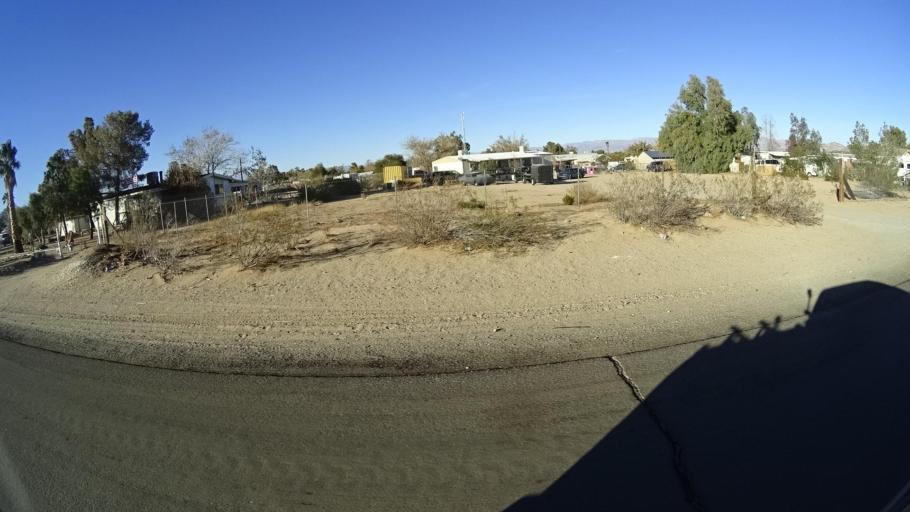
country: US
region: California
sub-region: Kern County
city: Ridgecrest
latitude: 35.6013
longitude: -117.6981
